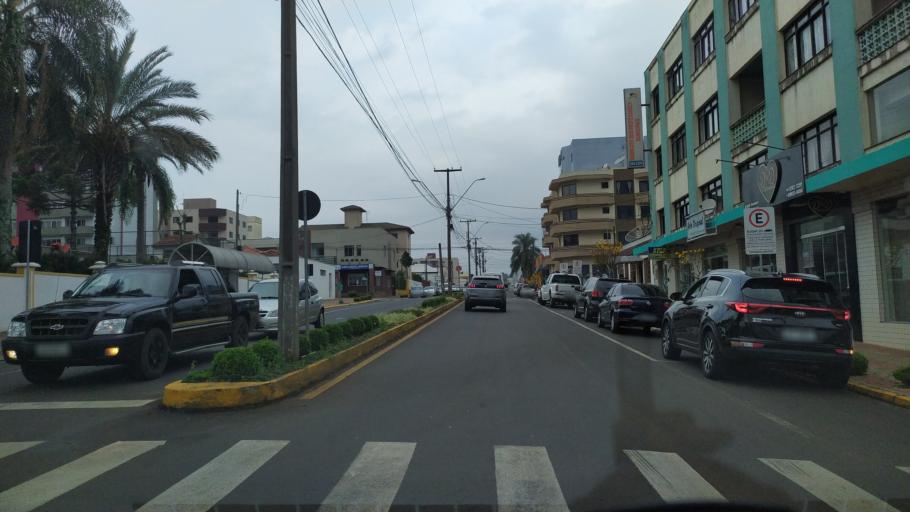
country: BR
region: Parana
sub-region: Palmas
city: Palmas
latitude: -26.4852
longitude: -51.9906
